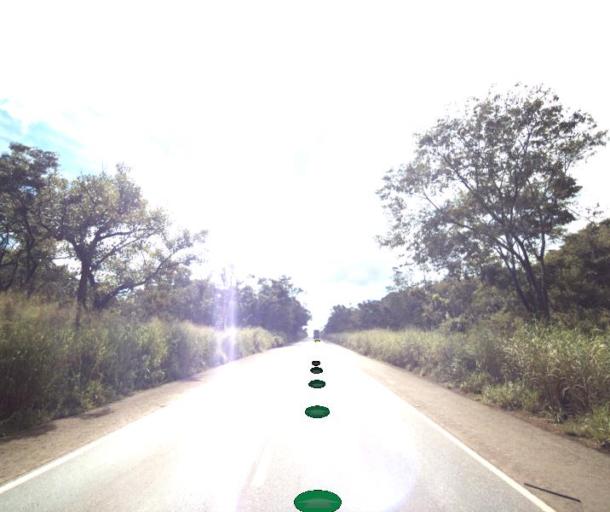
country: BR
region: Goias
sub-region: Jaragua
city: Jaragua
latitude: -15.9053
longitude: -49.2289
